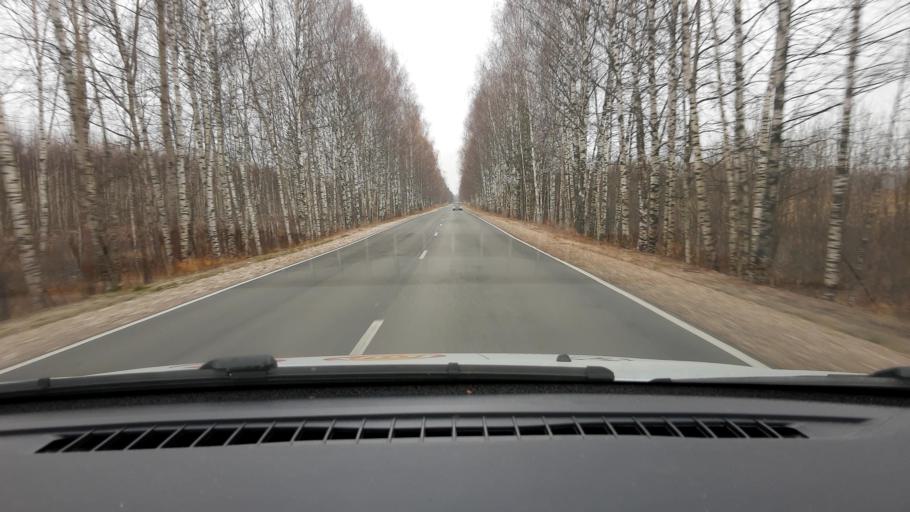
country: RU
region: Nizjnij Novgorod
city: Neklyudovo
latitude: 56.4901
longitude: 43.8614
